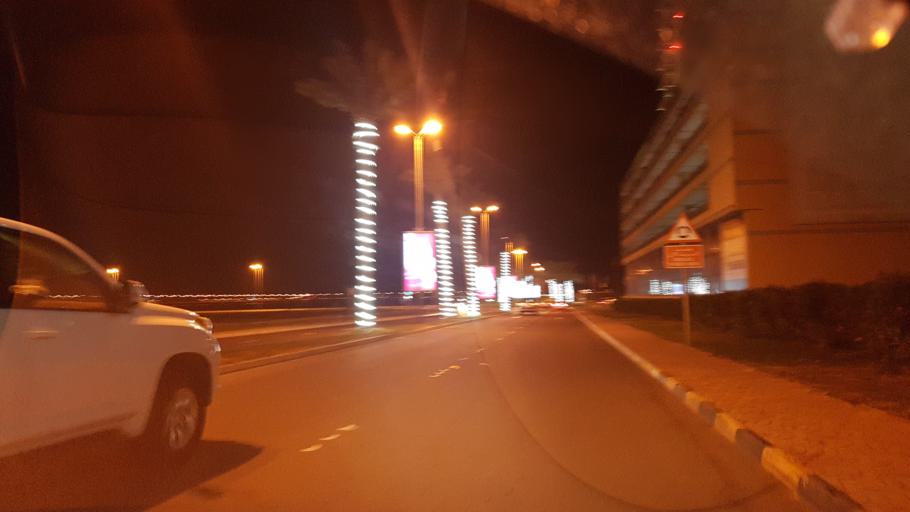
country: BH
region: Muharraq
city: Al Hadd
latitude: 26.2865
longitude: 50.6614
